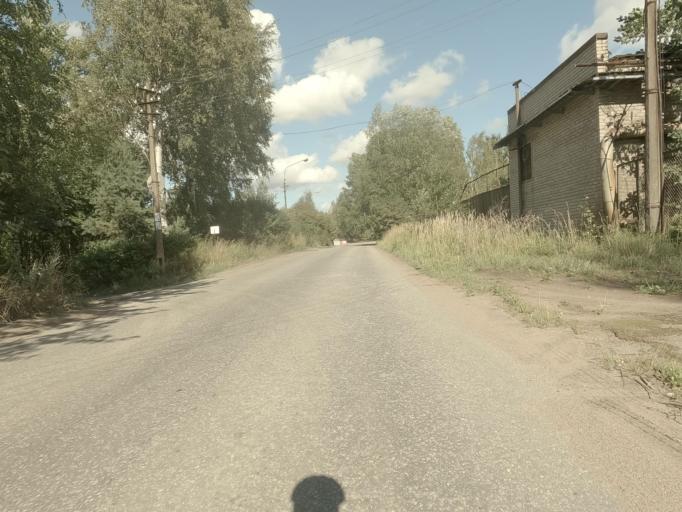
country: RU
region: Leningrad
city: Yanino Vtoroye
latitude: 59.9827
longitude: 30.5850
